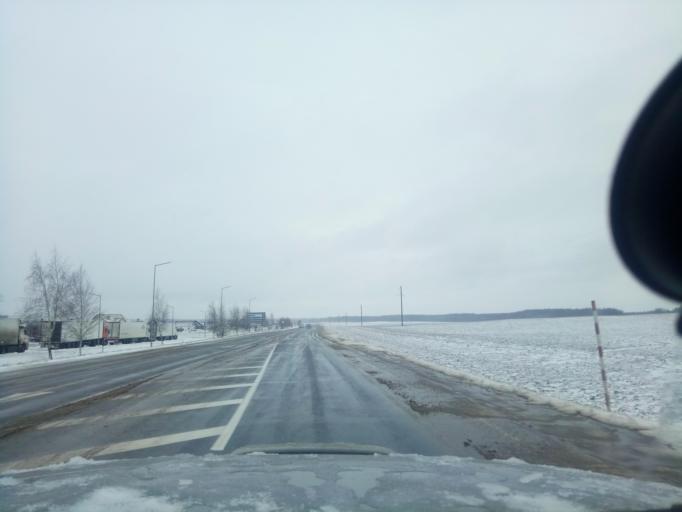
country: BY
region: Minsk
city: Nyasvizh
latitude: 53.2264
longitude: 26.6439
